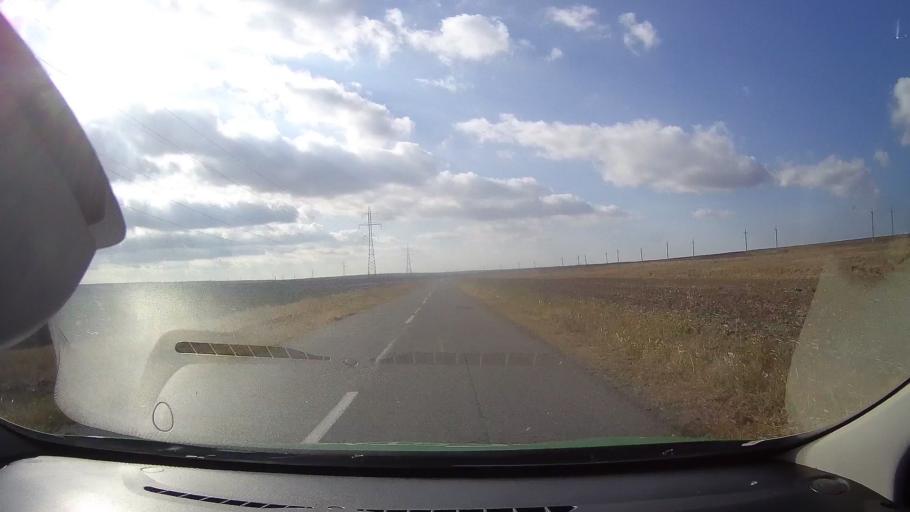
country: RO
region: Constanta
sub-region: Comuna Sacele
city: Sacele
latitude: 44.5053
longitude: 28.6676
